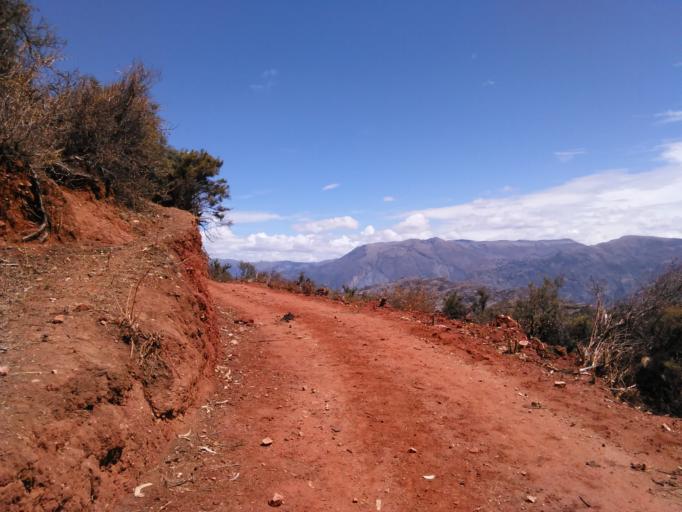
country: PE
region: Ayacucho
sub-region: Provincia de Victor Fajardo
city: Canaria
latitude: -13.8834
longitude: -73.9472
